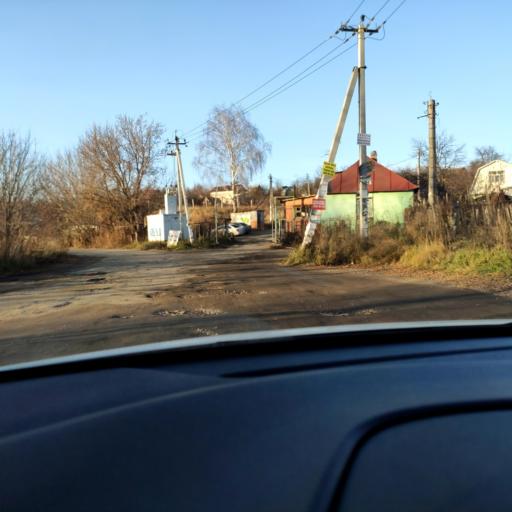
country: RU
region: Tatarstan
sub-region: Gorod Kazan'
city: Kazan
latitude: 55.8848
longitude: 49.0689
